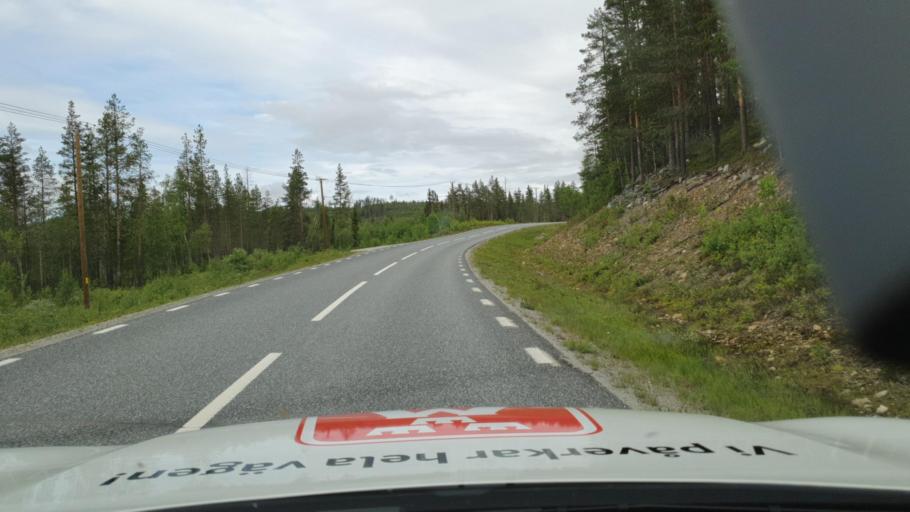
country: SE
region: Vaesterbotten
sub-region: Asele Kommun
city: Insjon
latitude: 64.3204
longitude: 17.7047
